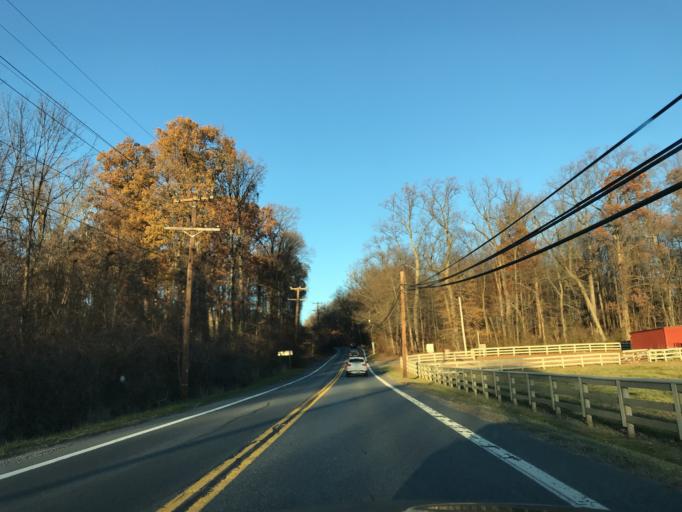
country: US
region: Maryland
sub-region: Howard County
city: Highland
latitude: 39.1719
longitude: -76.9646
